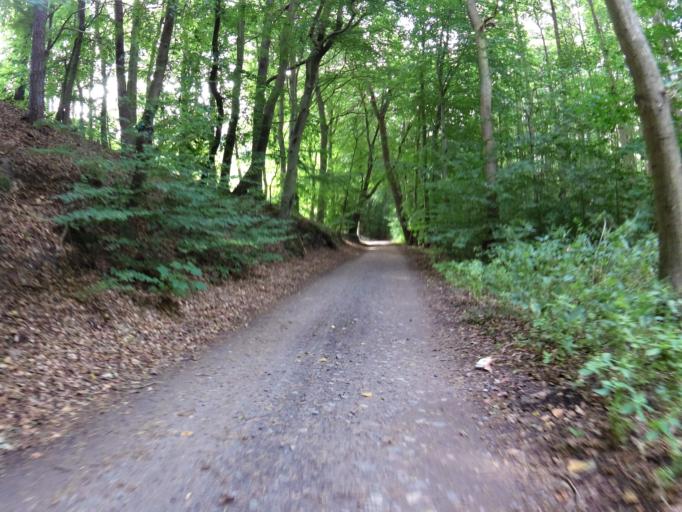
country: DE
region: Mecklenburg-Vorpommern
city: Seebad Bansin
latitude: 53.9733
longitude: 14.1076
